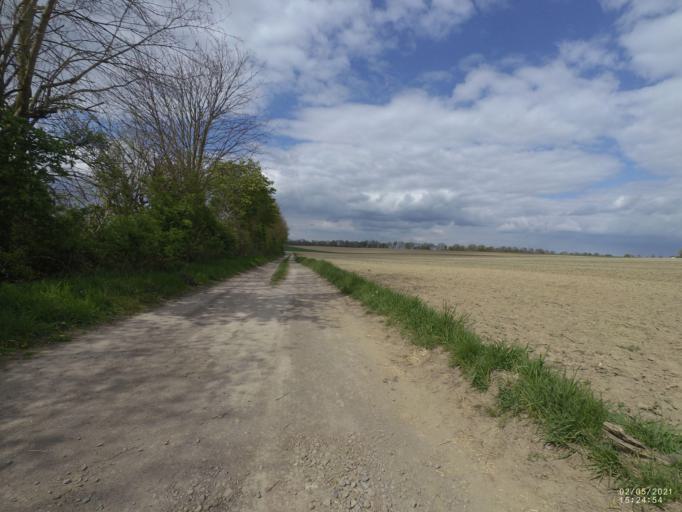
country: DE
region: Rheinland-Pfalz
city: Saffig
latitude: 50.3581
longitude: 7.4344
